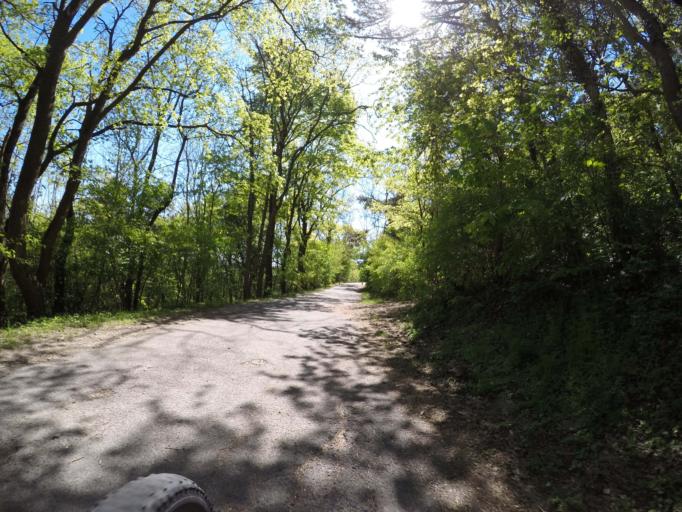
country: AT
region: Lower Austria
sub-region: Politischer Bezirk Modling
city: Modling
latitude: 48.0733
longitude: 16.2813
